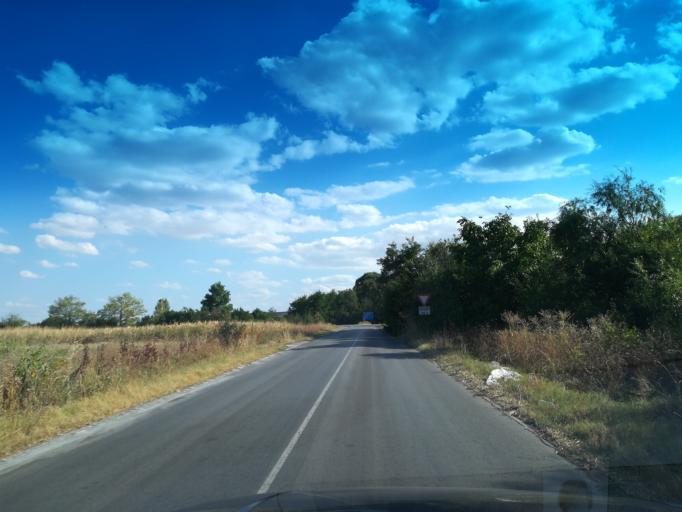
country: BG
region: Khaskovo
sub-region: Obshtina Mineralni Bani
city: Mineralni Bani
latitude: 42.0180
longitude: 25.4299
